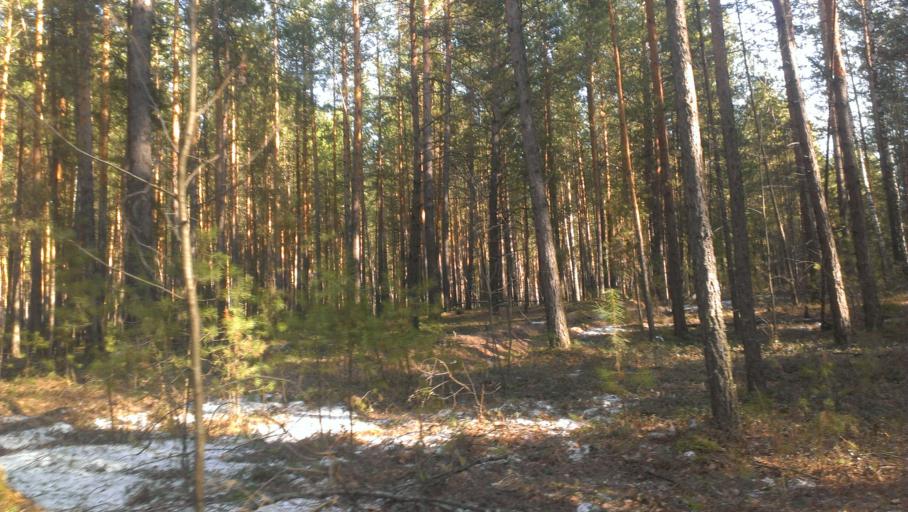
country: RU
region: Altai Krai
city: Yuzhnyy
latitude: 53.2829
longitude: 83.6972
